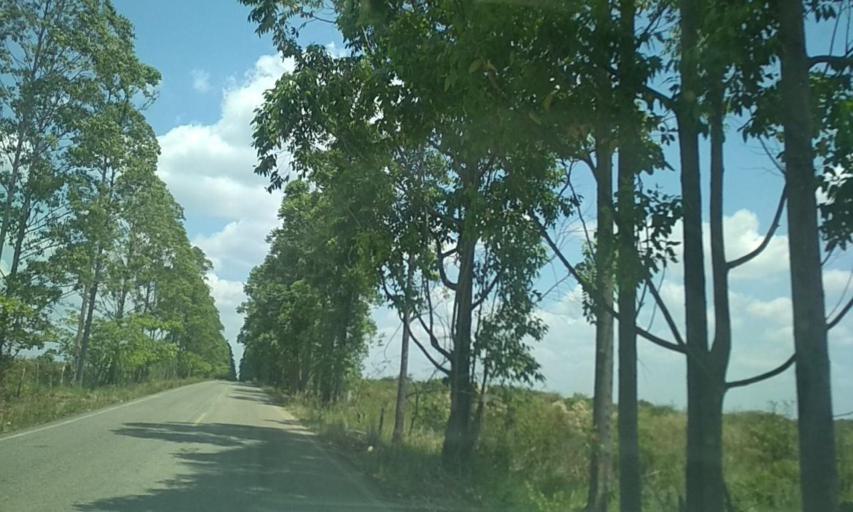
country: MX
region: Tabasco
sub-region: Huimanguillo
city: Francisco Rueda
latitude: 17.7656
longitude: -93.7944
